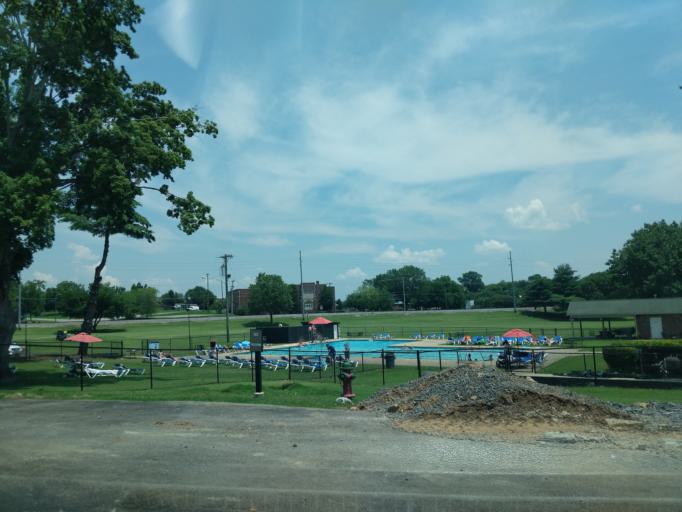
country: US
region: Tennessee
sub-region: Davidson County
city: Lakewood
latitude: 36.2488
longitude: -86.6457
